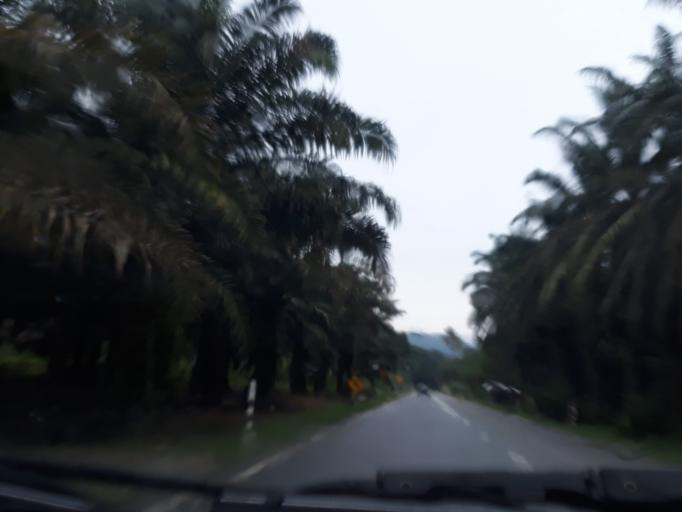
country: MY
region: Kedah
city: Kulim
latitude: 5.2364
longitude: 100.6025
